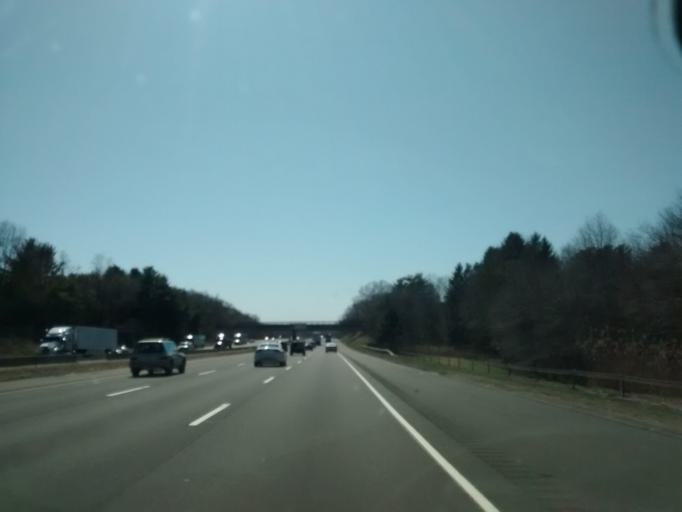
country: US
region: Connecticut
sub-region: Tolland County
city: Rockville
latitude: 41.8418
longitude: -72.4491
